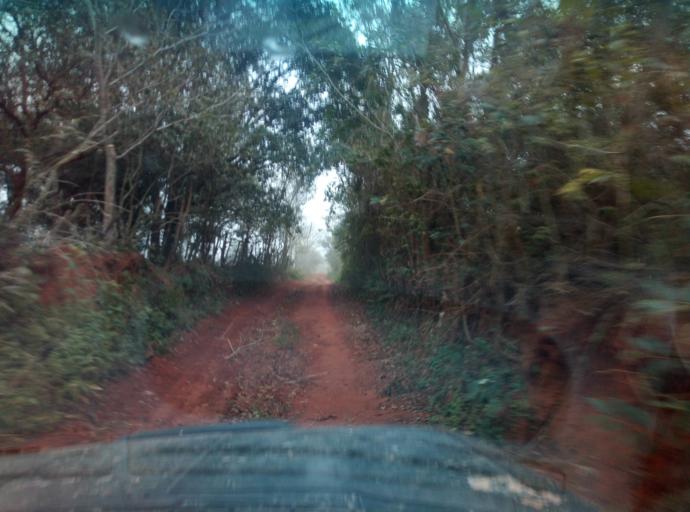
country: PY
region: Caaguazu
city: Doctor Cecilio Baez
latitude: -25.1511
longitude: -56.2540
